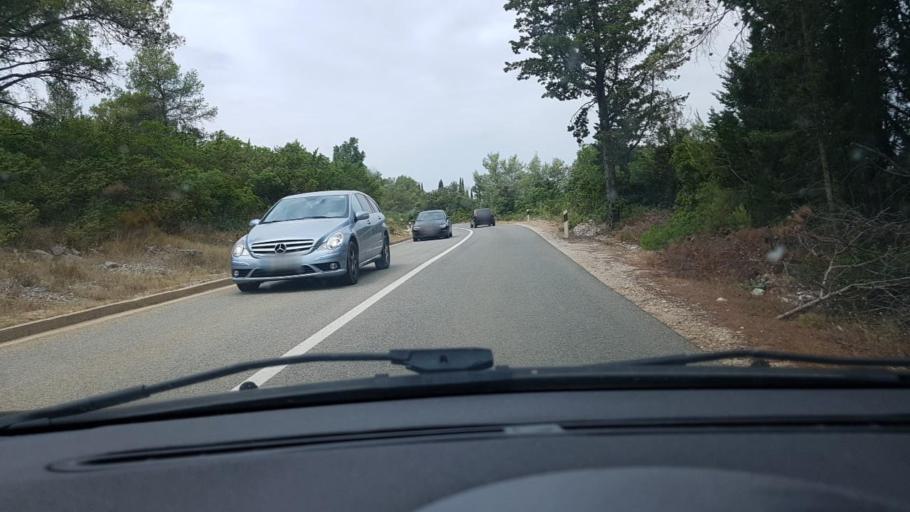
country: HR
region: Dubrovacko-Neretvanska
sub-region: Grad Korcula
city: Zrnovo
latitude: 42.9379
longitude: 17.0941
